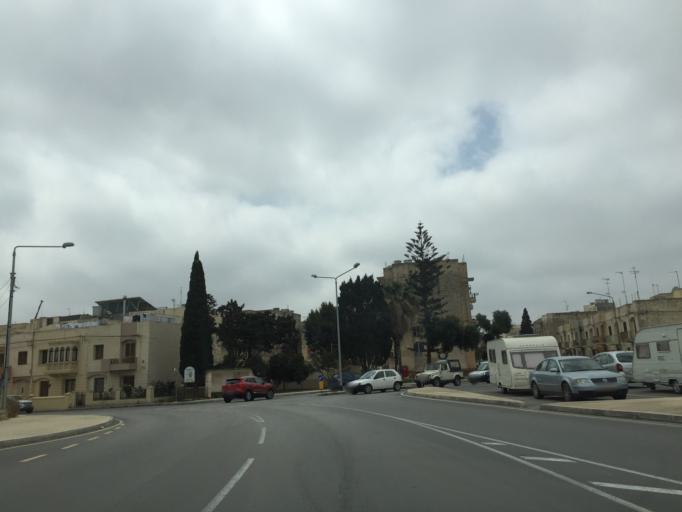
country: MT
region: Ir-Rabat
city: Rabat
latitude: 35.8841
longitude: 14.3912
